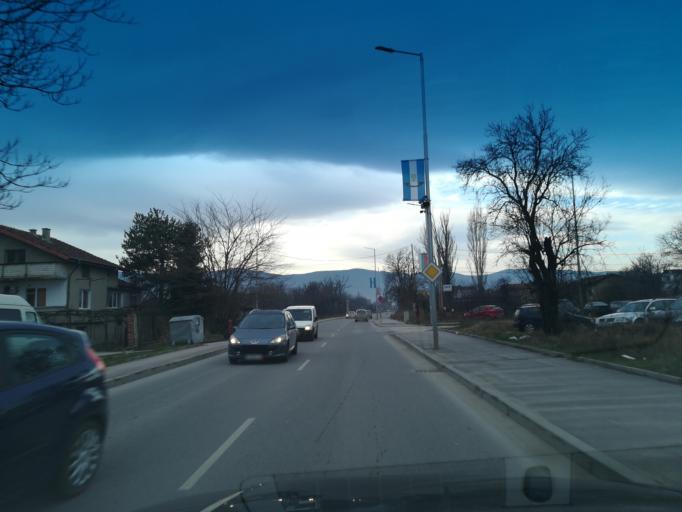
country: BG
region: Plovdiv
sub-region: Obshtina Plovdiv
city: Plovdiv
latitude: 42.1178
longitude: 24.7138
